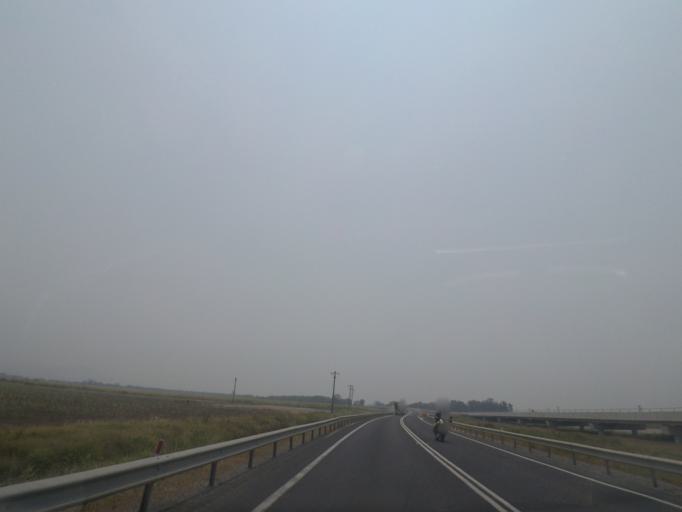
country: AU
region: New South Wales
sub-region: Clarence Valley
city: Maclean
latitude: -29.4101
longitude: 153.2418
